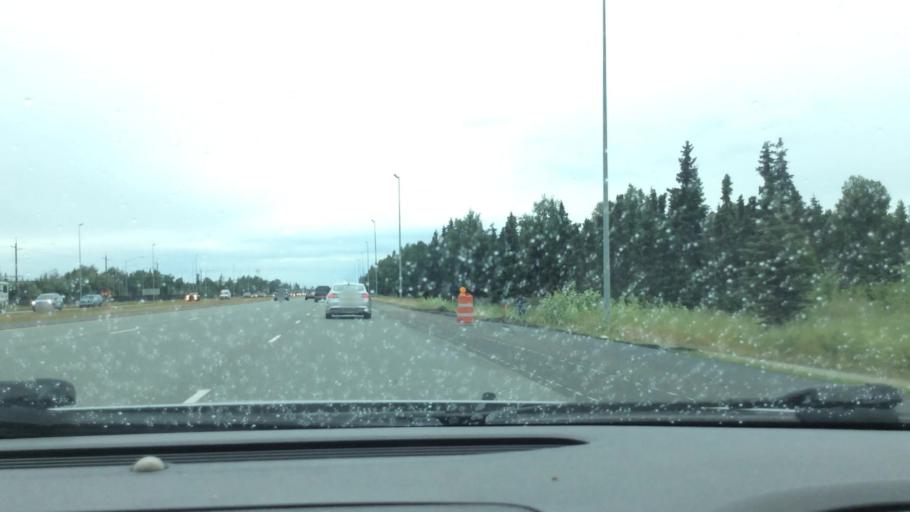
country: US
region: Alaska
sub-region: Anchorage Municipality
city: Elmendorf Air Force Base
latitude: 61.2248
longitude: -149.7475
